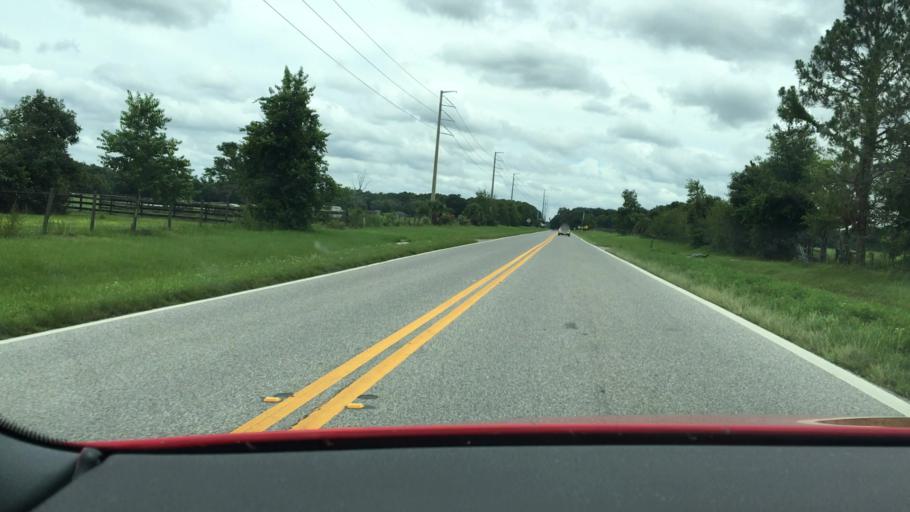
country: US
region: Florida
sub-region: Lake County
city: Eustis
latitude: 28.8693
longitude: -81.6585
